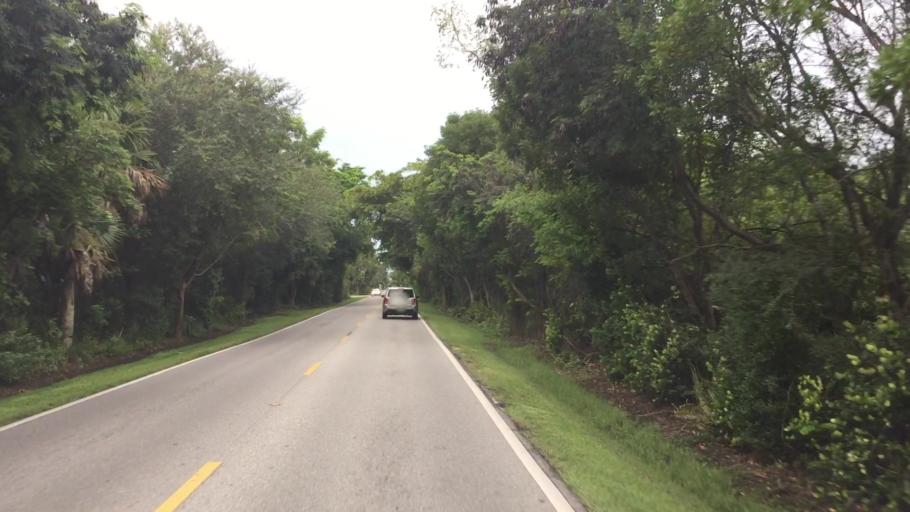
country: US
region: Florida
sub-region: Lee County
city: Sanibel
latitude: 26.4409
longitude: -82.0610
